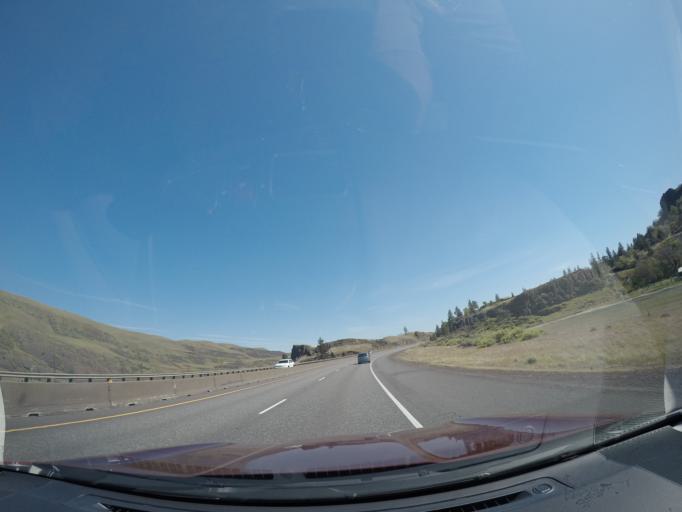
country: US
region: Oregon
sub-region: Wasco County
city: Chenoweth
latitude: 45.6655
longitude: -121.2238
